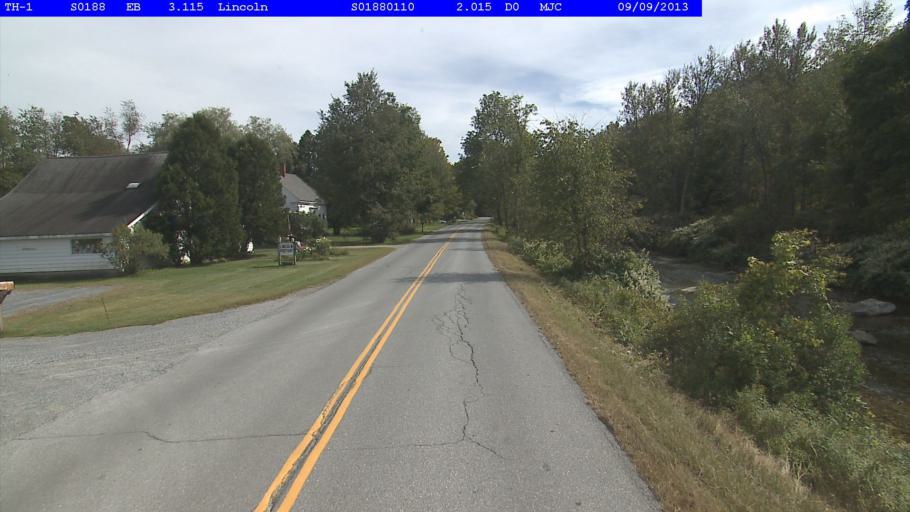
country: US
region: Vermont
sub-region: Addison County
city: Bristol
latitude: 44.1082
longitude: -73.0000
